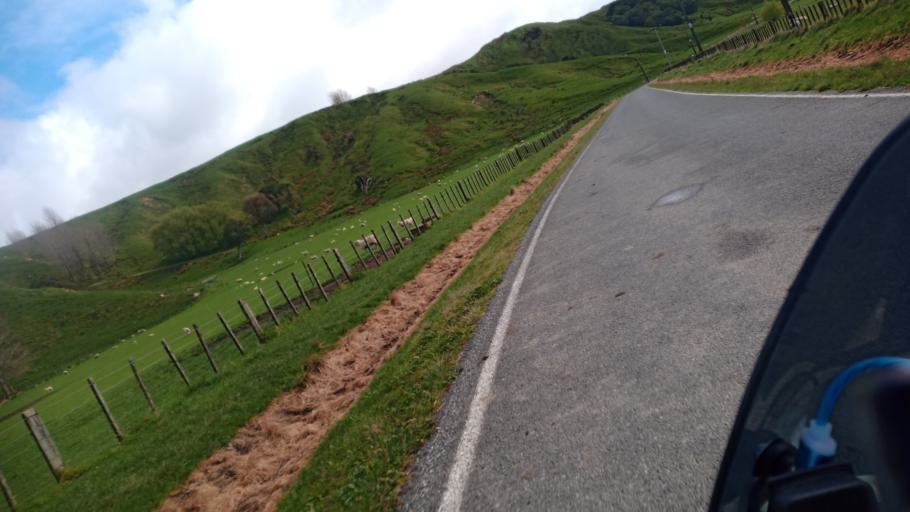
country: NZ
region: Gisborne
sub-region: Gisborne District
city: Gisborne
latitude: -38.5753
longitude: 178.1714
